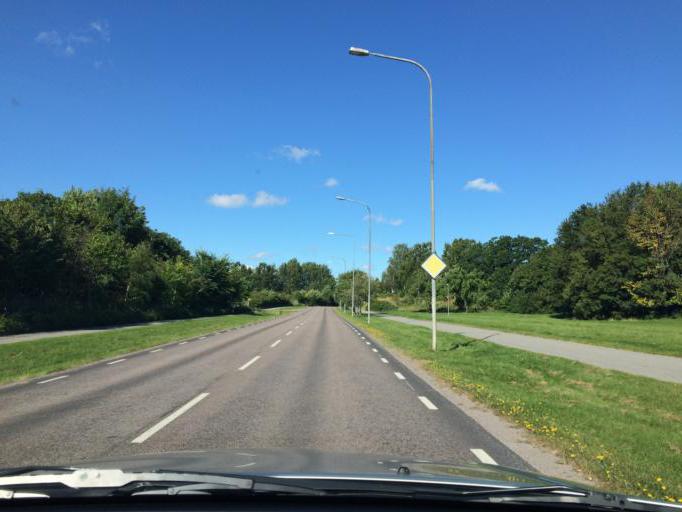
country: SE
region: Vaestmanland
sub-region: Vasteras
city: Vasteras
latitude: 59.5932
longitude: 16.6033
